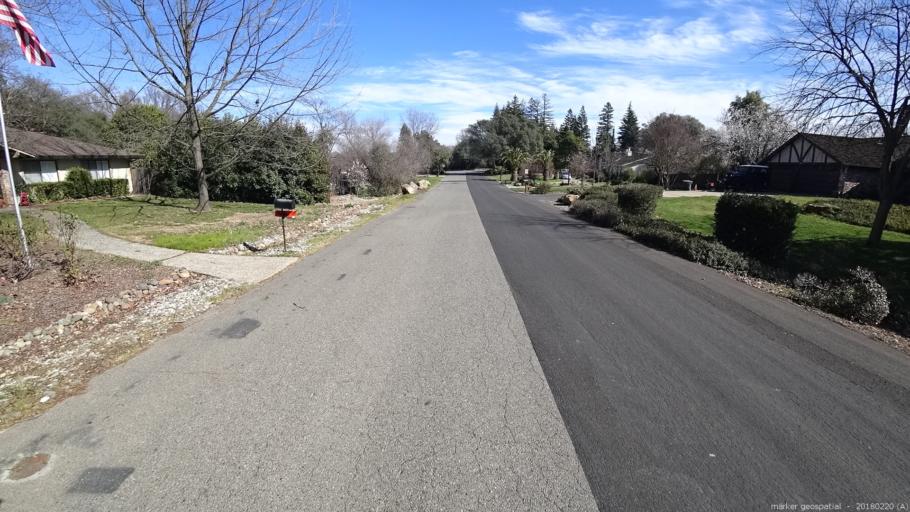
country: US
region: California
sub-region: Sacramento County
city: Orangevale
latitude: 38.6961
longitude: -121.2267
